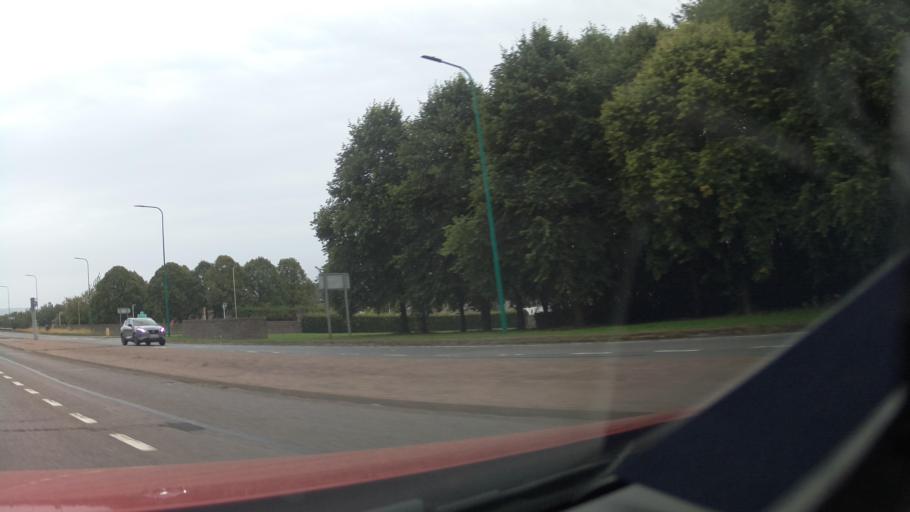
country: GB
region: Scotland
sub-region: Angus
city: Muirhead
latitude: 56.4615
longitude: -3.0549
